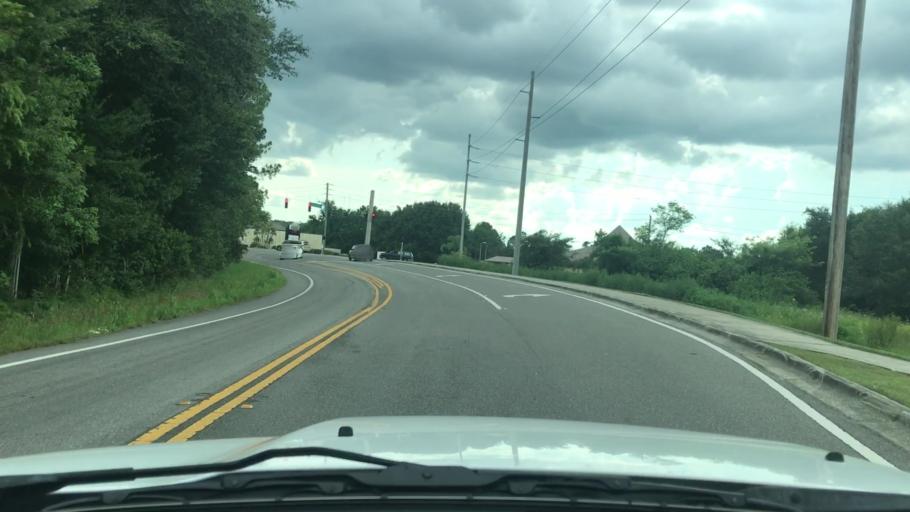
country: US
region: Florida
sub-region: Polk County
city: Cypress Gardens
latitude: 28.0151
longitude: -81.6763
